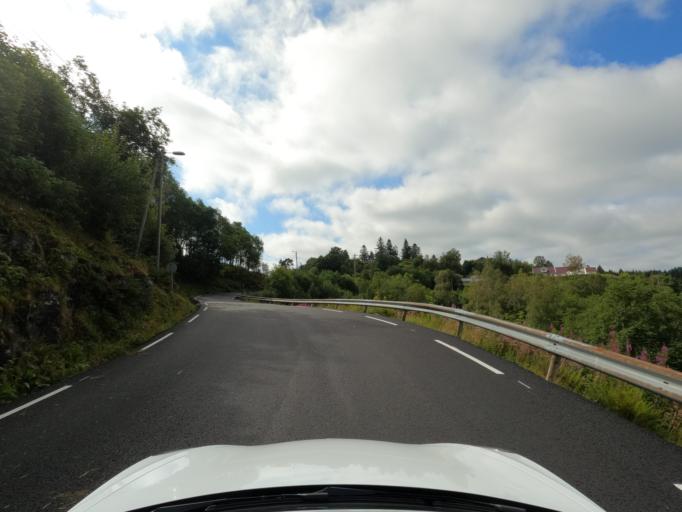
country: NO
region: Hordaland
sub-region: Os
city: Syfteland
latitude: 60.3054
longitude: 5.4180
